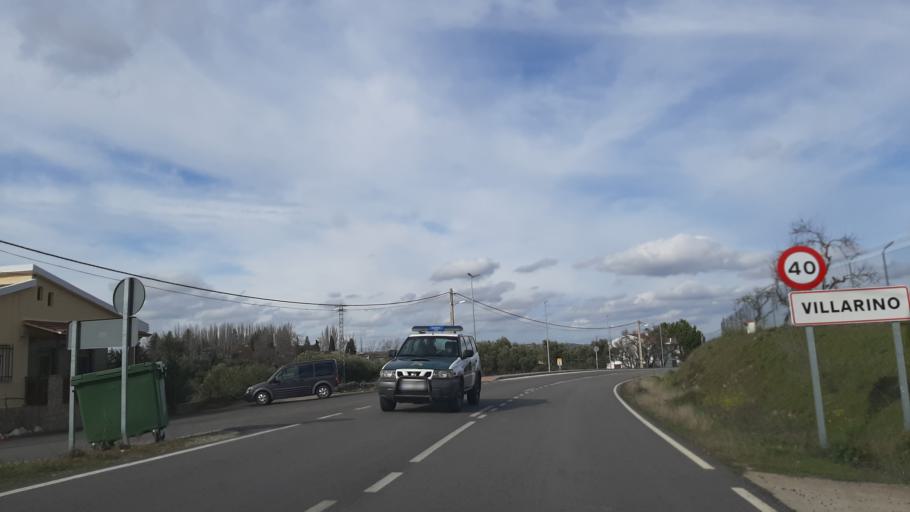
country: ES
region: Castille and Leon
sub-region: Provincia de Salamanca
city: Villarino de los Aires
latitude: 41.2629
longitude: -6.4717
